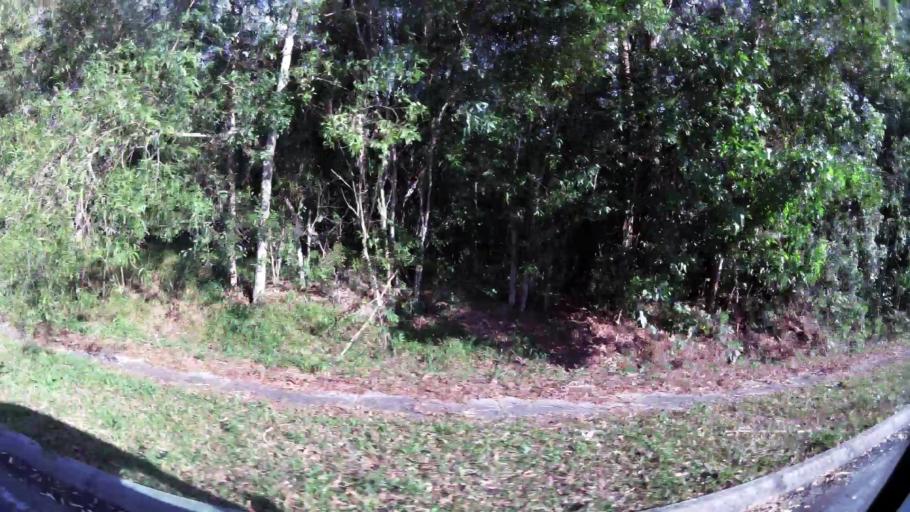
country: BN
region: Brunei and Muara
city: Bandar Seri Begawan
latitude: 4.9844
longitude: 114.9724
